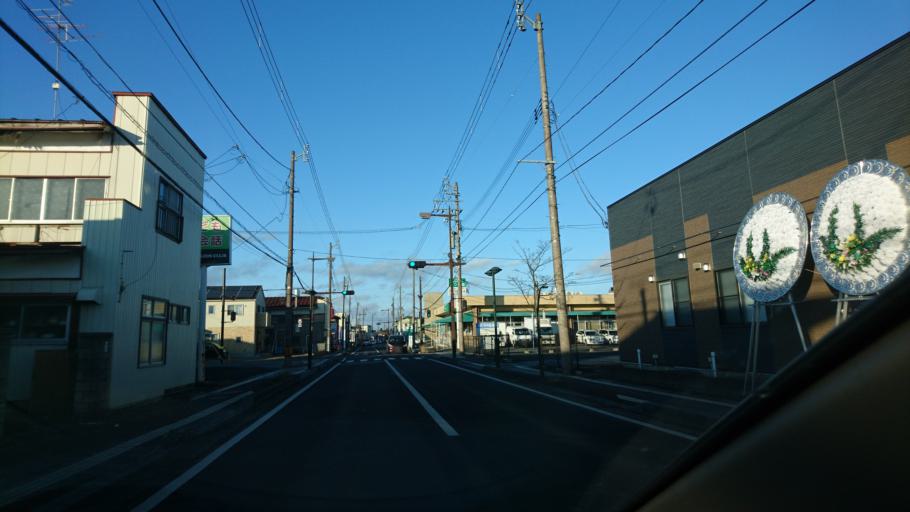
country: JP
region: Miyagi
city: Furukawa
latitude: 38.5694
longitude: 140.8595
